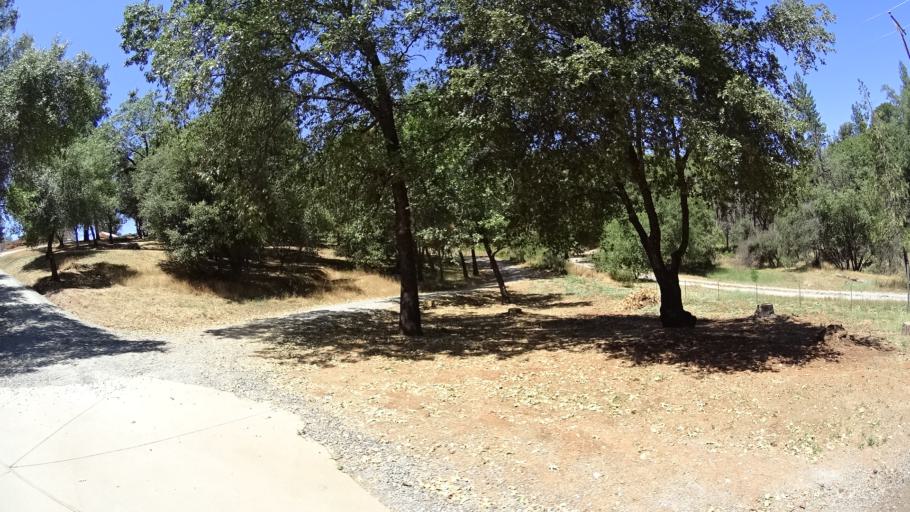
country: US
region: California
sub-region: Calaveras County
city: Mountain Ranch
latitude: 38.2388
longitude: -120.5751
